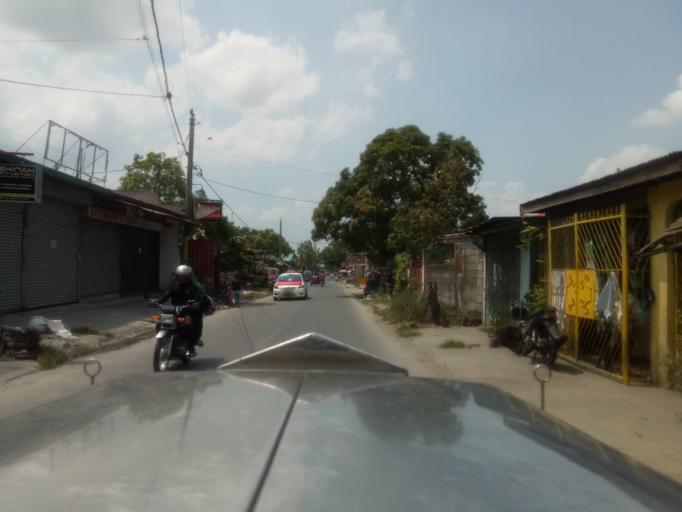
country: PH
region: Calabarzon
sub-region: Province of Cavite
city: Dasmarinas
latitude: 14.3161
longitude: 120.9766
